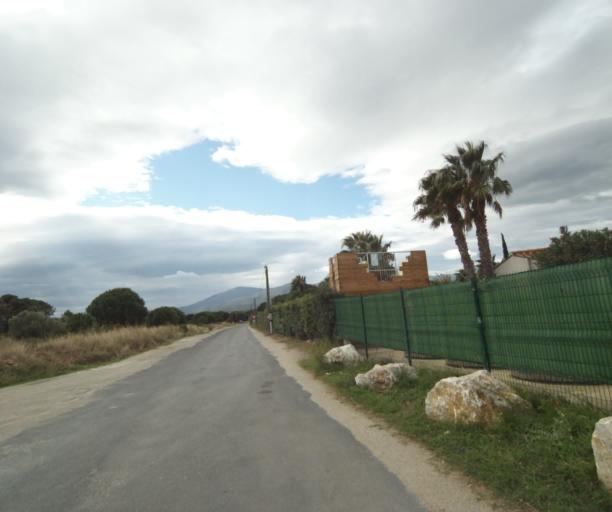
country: FR
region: Languedoc-Roussillon
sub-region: Departement des Pyrenees-Orientales
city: Argelers
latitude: 42.5720
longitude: 3.0412
